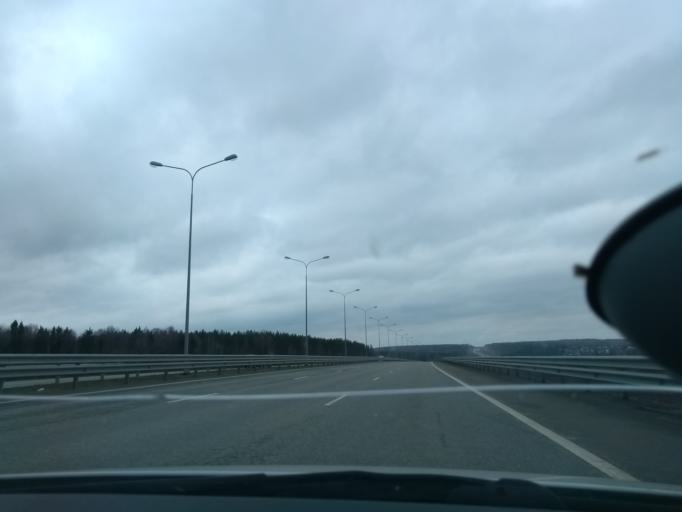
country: RU
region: Perm
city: Bershet'
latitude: 57.7074
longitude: 56.3680
